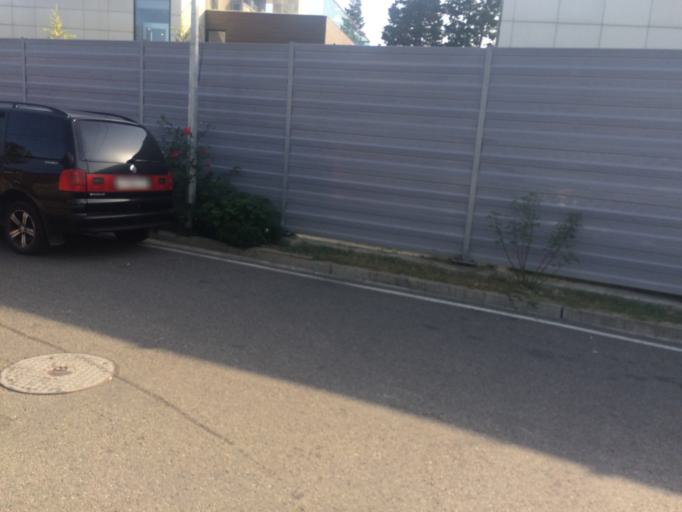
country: RU
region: Krasnodarskiy
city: Adler
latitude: 43.3921
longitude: 39.9790
